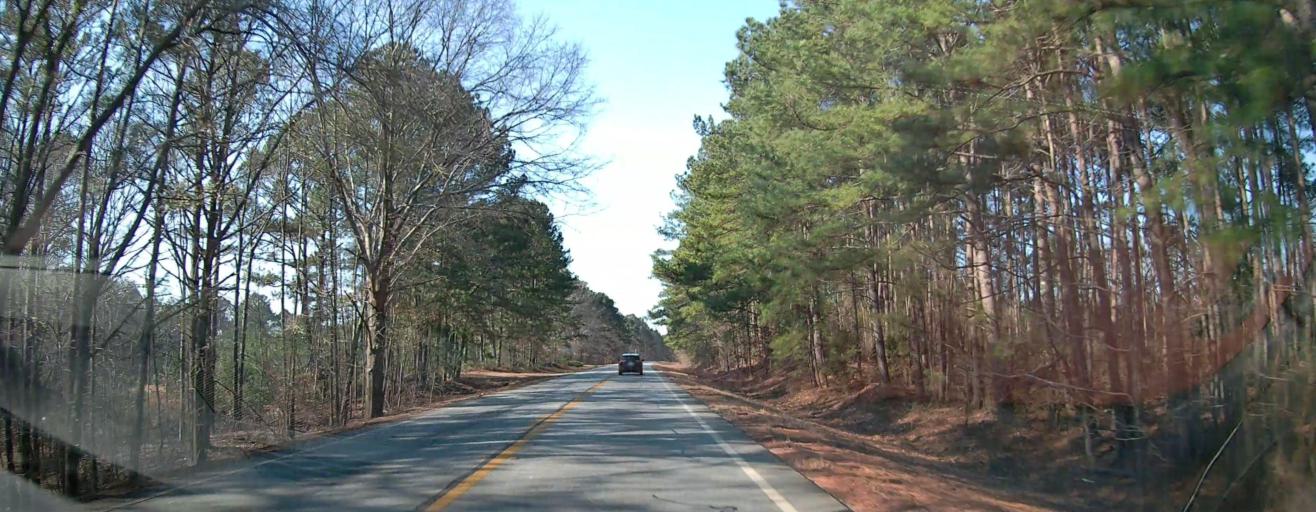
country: US
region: Georgia
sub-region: Butts County
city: Indian Springs
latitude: 33.2261
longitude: -83.8731
